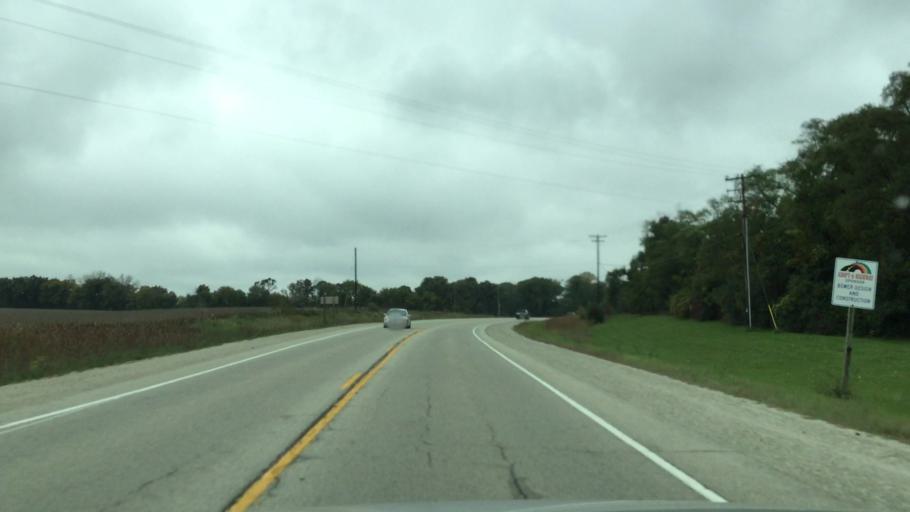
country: US
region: Wisconsin
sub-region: Racine County
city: Eagle Lake
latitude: 42.7401
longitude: -88.0920
